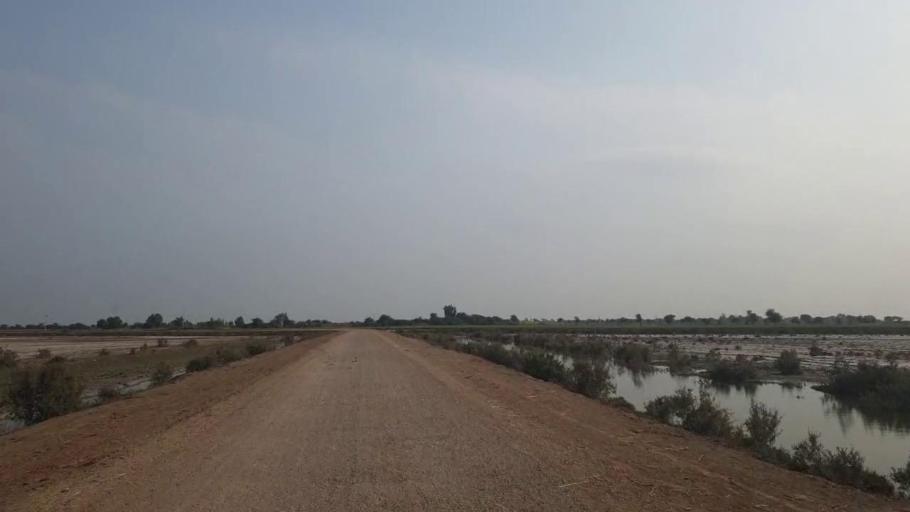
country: PK
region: Sindh
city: Badin
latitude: 24.6014
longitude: 68.6969
